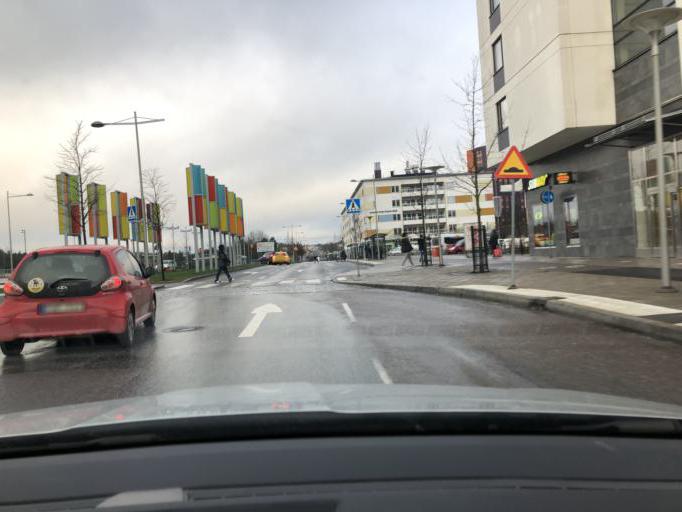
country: SE
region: Stockholm
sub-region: Botkyrka Kommun
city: Tullinge
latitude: 59.2222
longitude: 17.9391
